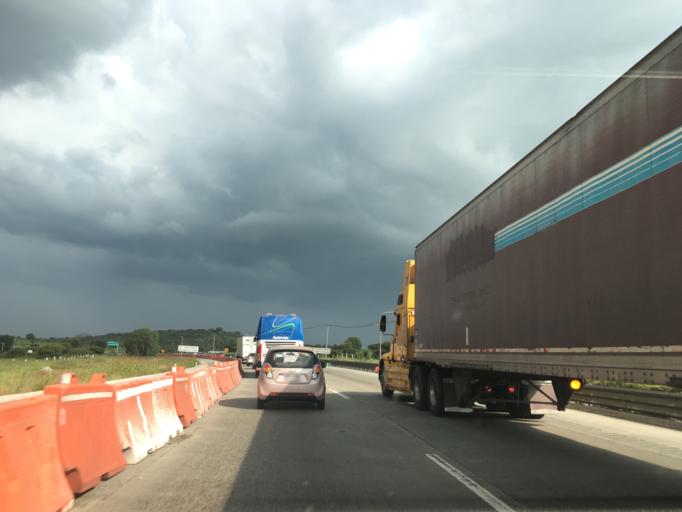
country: MX
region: Hidalgo
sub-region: Tepeji del Rio de Ocampo
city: Santiago Tlapanaloya
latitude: 19.8690
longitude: -99.3376
